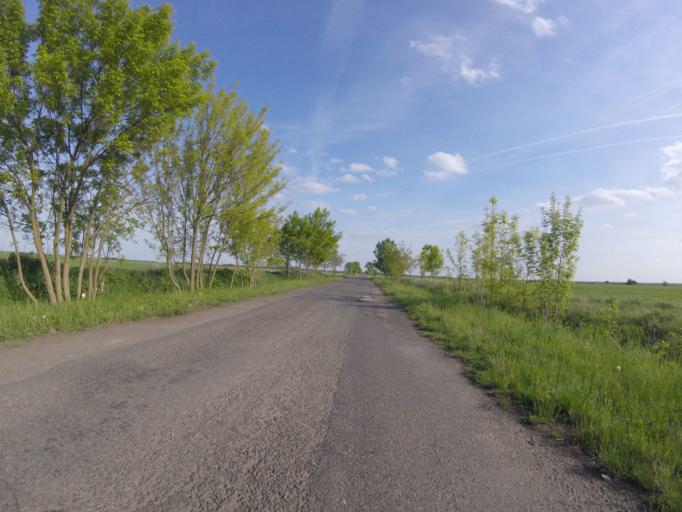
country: HU
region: Pest
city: Tapiogyorgye
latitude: 47.2991
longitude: 19.9818
